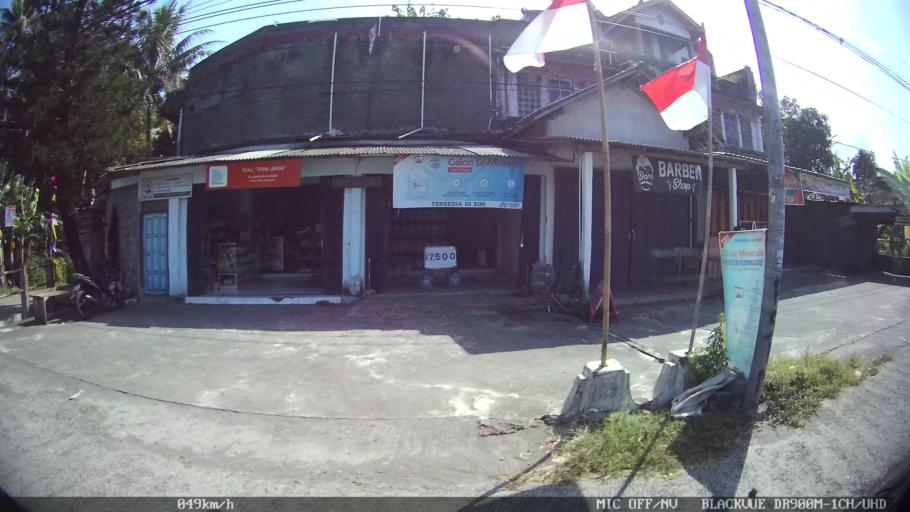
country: ID
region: Daerah Istimewa Yogyakarta
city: Srandakan
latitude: -7.9308
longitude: 110.2097
